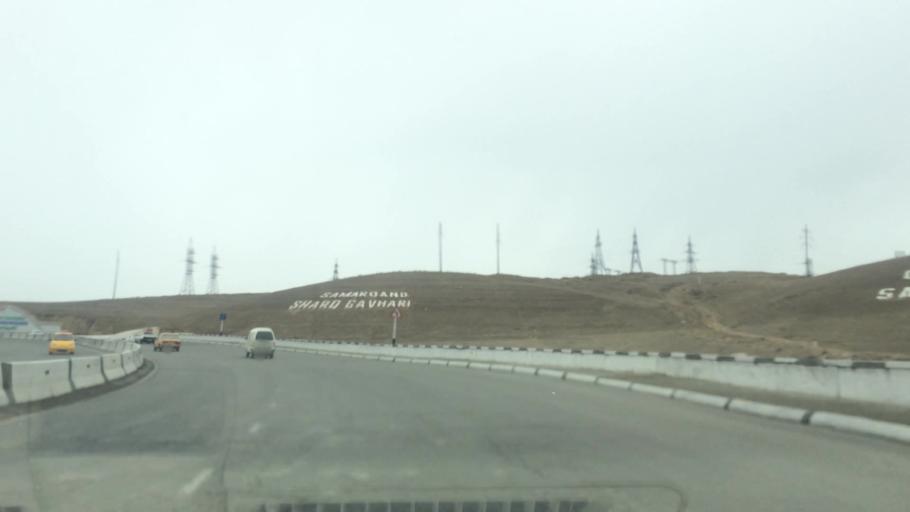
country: UZ
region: Samarqand
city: Jomboy
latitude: 39.6886
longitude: 67.0526
